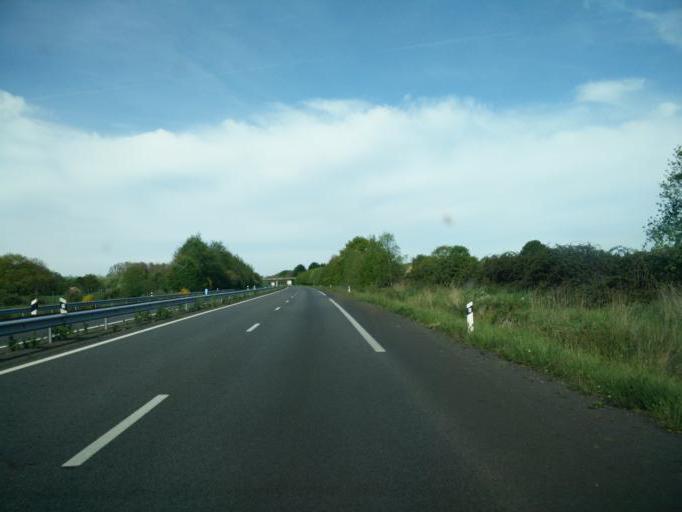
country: FR
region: Brittany
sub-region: Departement d'Ille-et-Vilaine
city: Roz-sur-Couesnon
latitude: 48.5669
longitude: -1.5750
